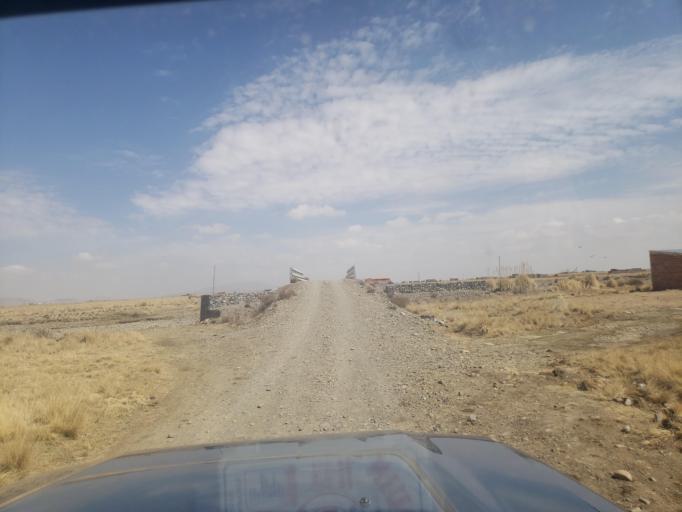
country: BO
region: La Paz
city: Batallas
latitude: -16.4287
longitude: -68.3947
